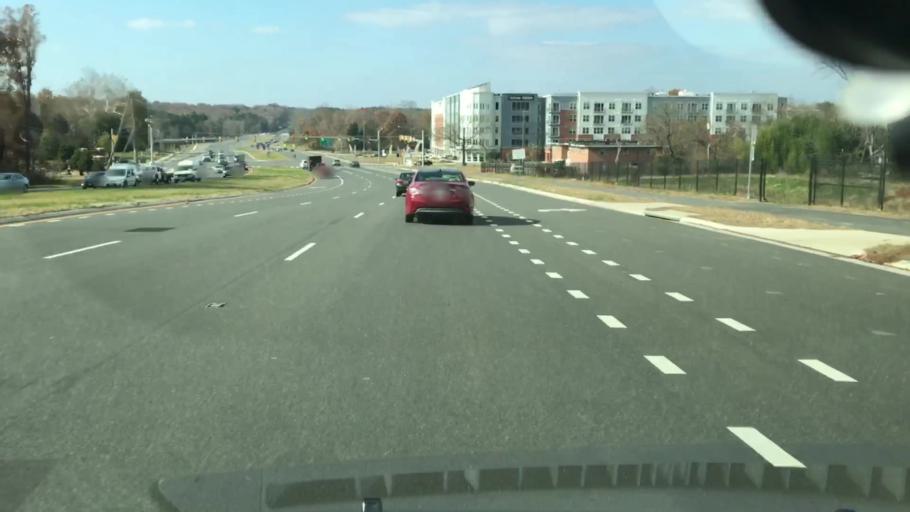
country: US
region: Virginia
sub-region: Fairfax County
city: Fort Belvoir
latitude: 38.7090
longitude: -77.1569
